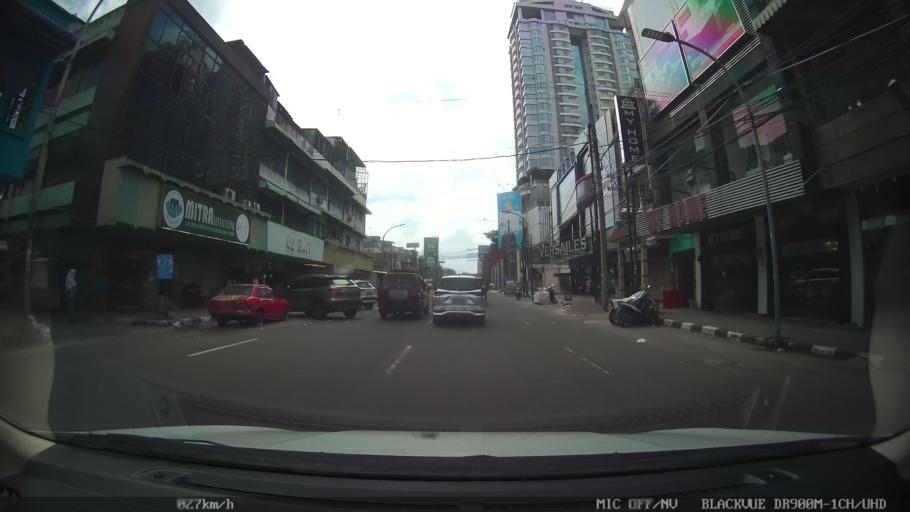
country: ID
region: North Sumatra
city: Medan
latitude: 3.5841
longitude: 98.6687
